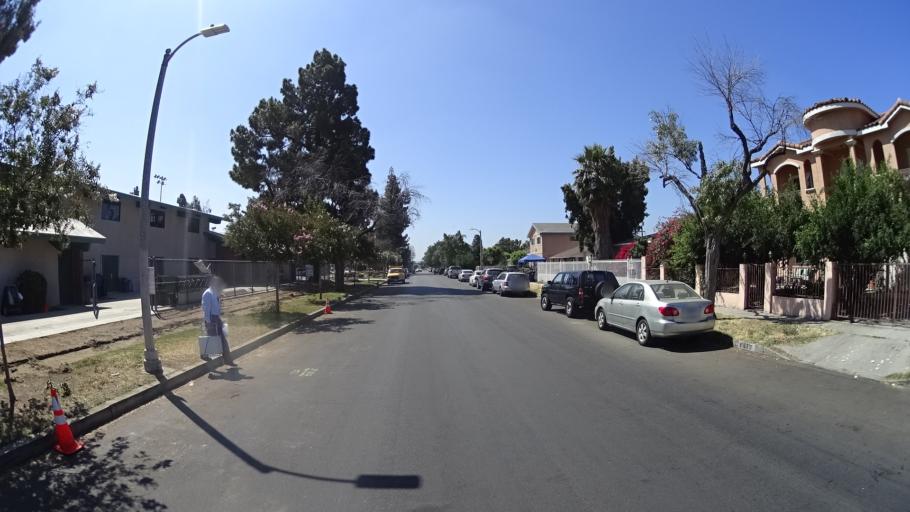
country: US
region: California
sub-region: Los Angeles County
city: Van Nuys
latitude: 34.2275
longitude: -118.4420
